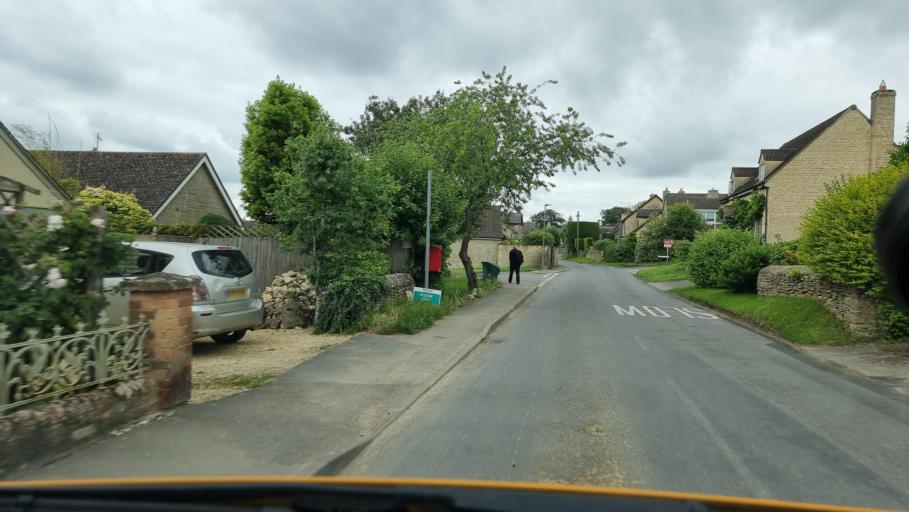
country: GB
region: England
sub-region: Oxfordshire
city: North Leigh
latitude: 51.8156
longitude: -1.4438
